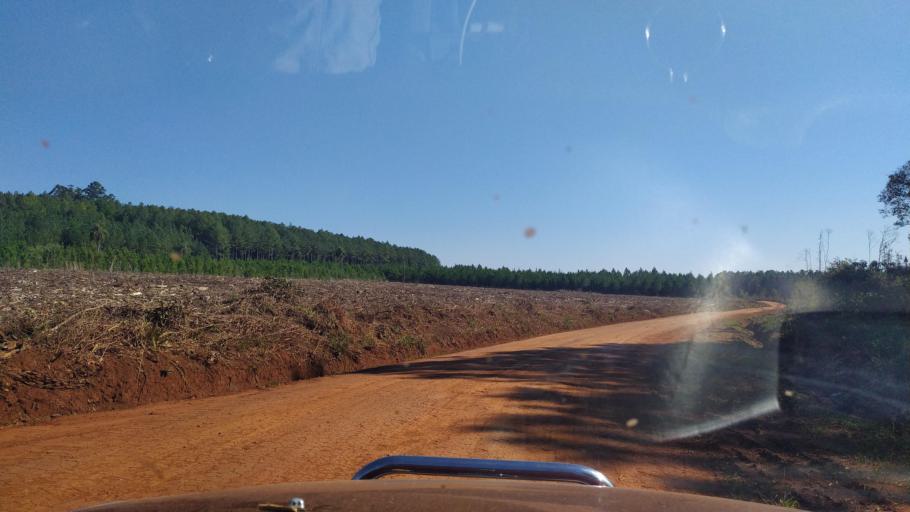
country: AR
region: Misiones
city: El Alcazar
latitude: -26.7355
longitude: -54.6632
